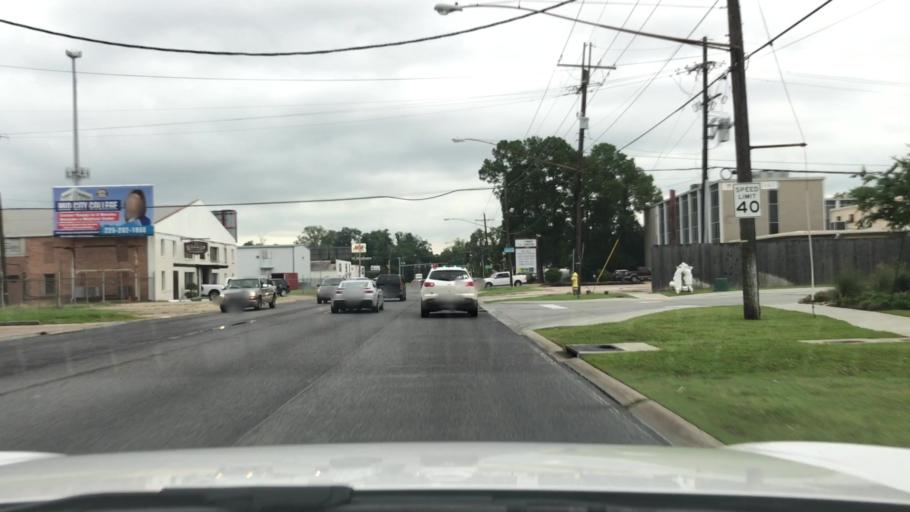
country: US
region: Louisiana
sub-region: East Baton Rouge Parish
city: Baton Rouge
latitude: 30.4514
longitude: -91.1390
